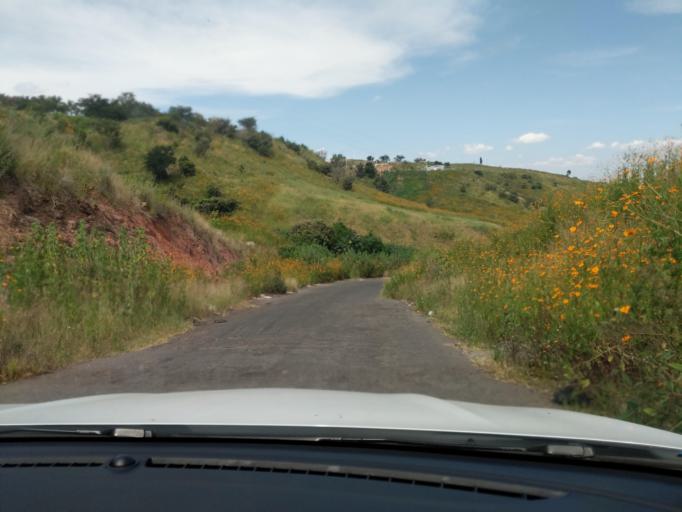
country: MX
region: Jalisco
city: Tonala
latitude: 20.6304
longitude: -103.2213
